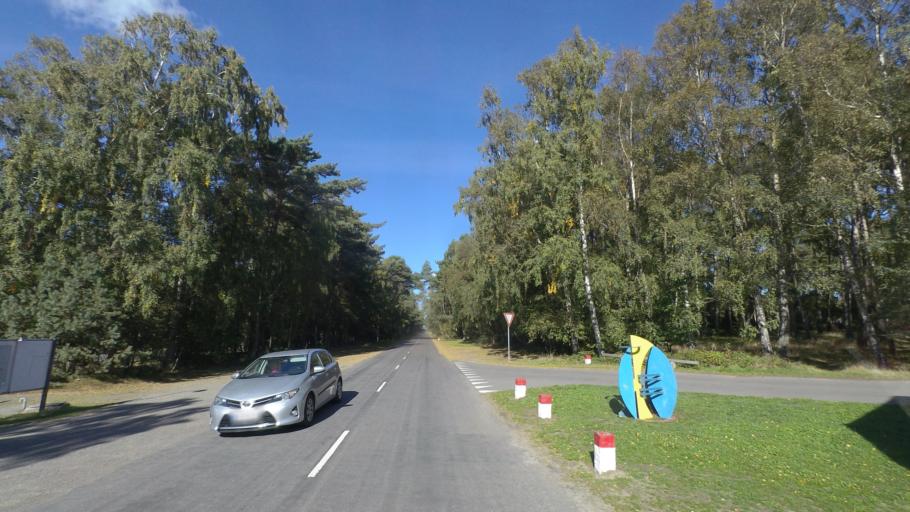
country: DK
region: Capital Region
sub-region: Bornholm Kommune
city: Nexo
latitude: 54.9936
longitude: 15.0779
